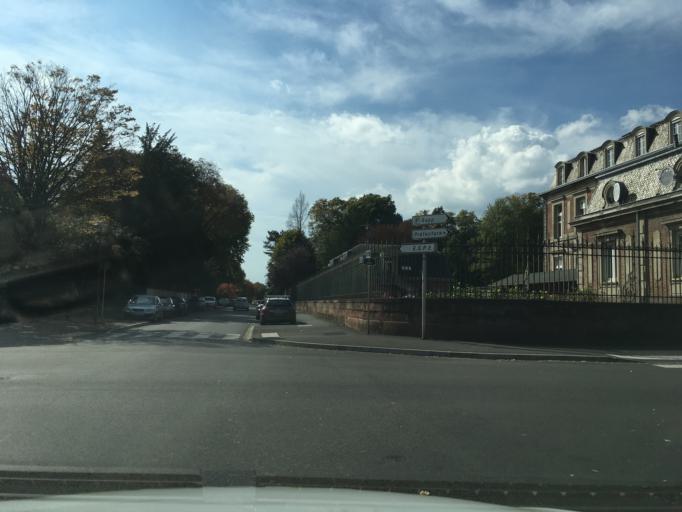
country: FR
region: Alsace
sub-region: Departement du Haut-Rhin
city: Colmar
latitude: 48.0743
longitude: 7.3527
